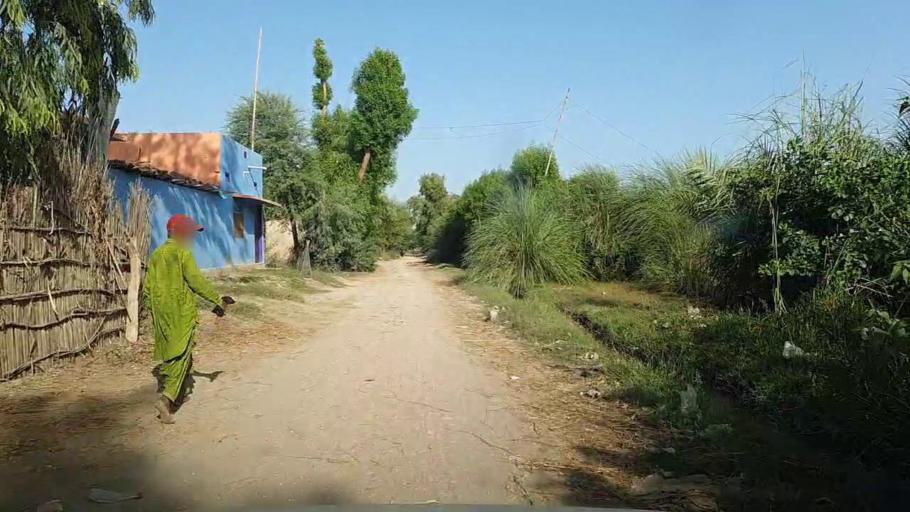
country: PK
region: Sindh
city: Kario
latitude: 24.5996
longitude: 68.5250
